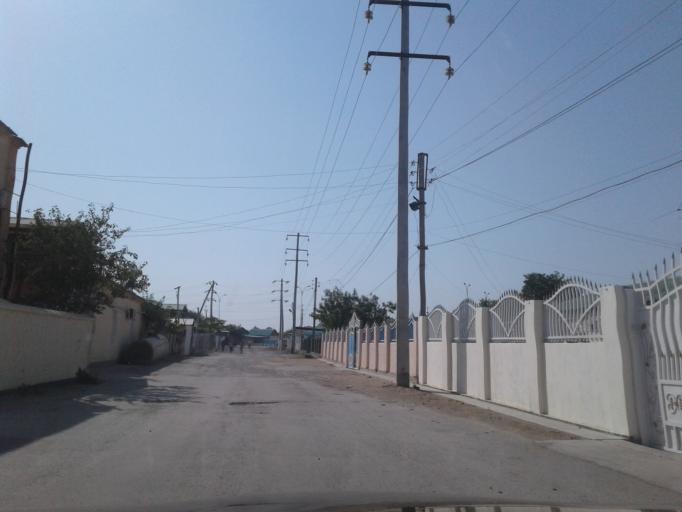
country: TM
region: Ahal
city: Ashgabat
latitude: 37.9736
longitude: 58.4338
